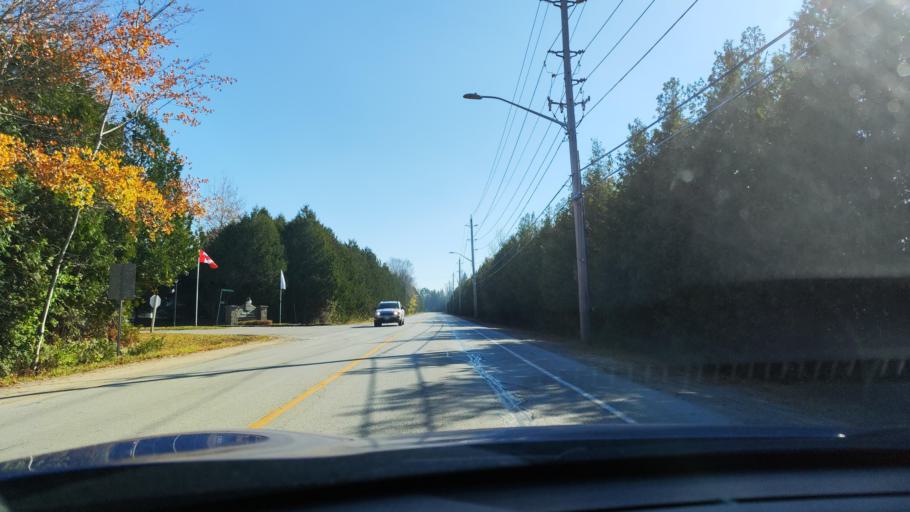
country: CA
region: Ontario
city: Wasaga Beach
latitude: 44.5045
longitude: -79.9915
